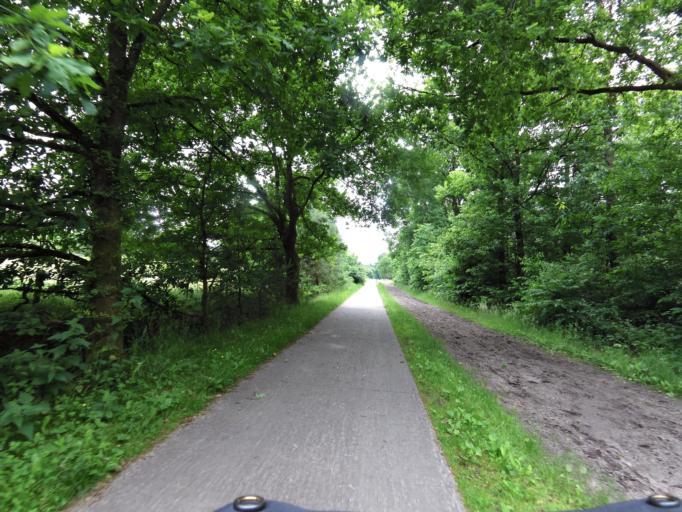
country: NL
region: Gelderland
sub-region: Gemeente Apeldoorn
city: Loenen
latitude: 52.1479
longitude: 6.0125
